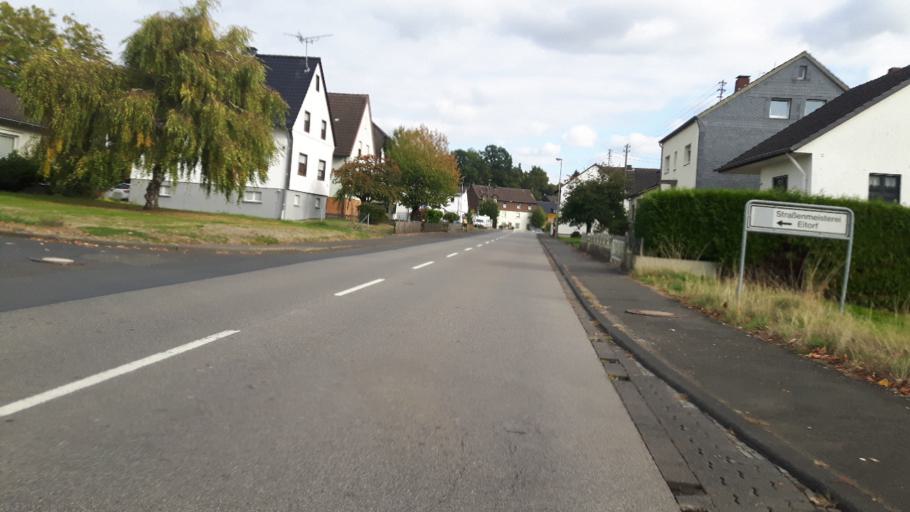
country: DE
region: North Rhine-Westphalia
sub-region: Regierungsbezirk Koln
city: Eitorf
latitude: 50.7740
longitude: 7.4774
